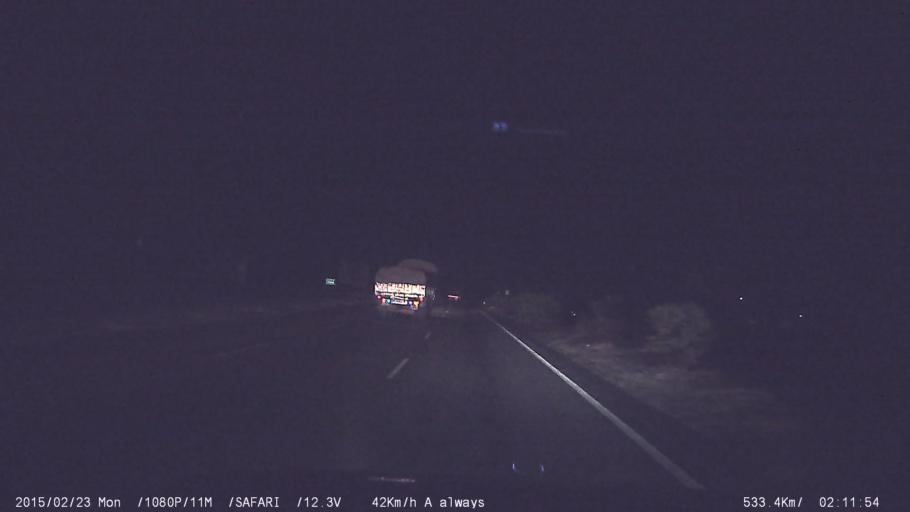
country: IN
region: Tamil Nadu
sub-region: Krishnagiri
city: Kelamangalam
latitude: 12.6782
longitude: 77.9636
